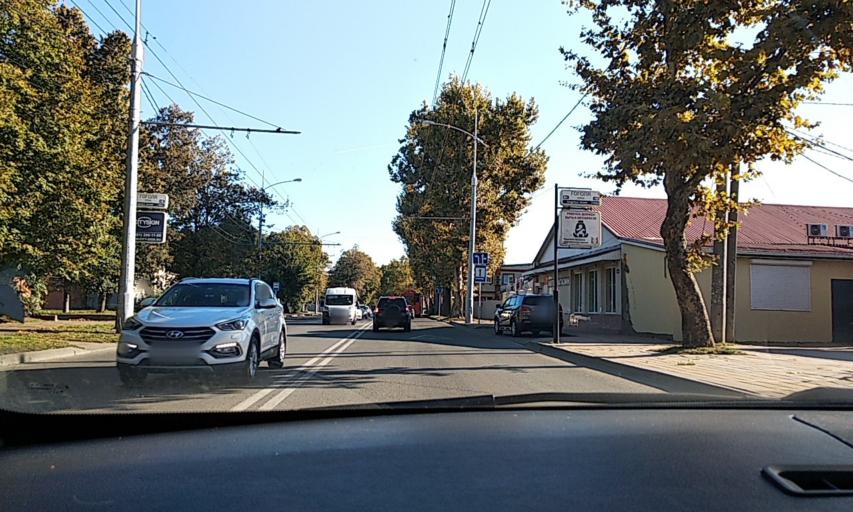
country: RU
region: Krasnodarskiy
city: Pashkovskiy
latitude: 45.0178
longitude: 39.0990
